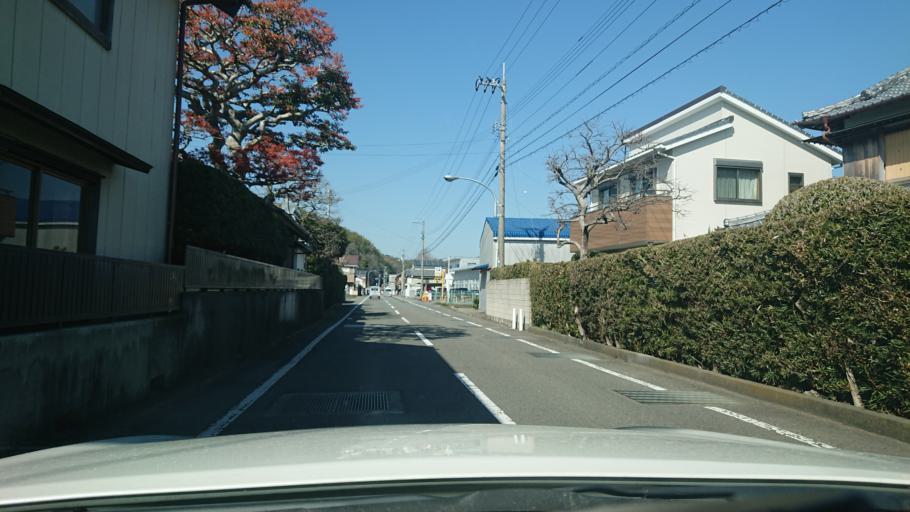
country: JP
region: Tokushima
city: Komatsushimacho
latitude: 33.9660
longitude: 134.6063
